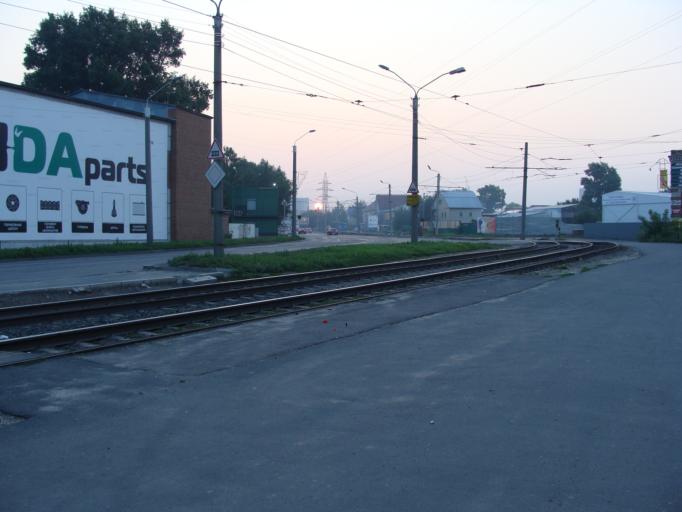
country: RU
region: Altai Krai
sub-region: Gorod Barnaulskiy
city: Barnaul
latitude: 53.3390
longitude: 83.7448
